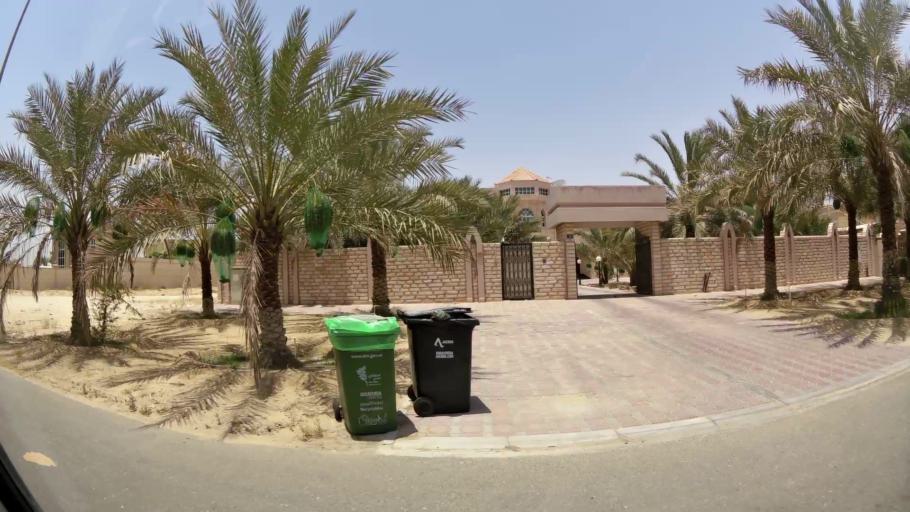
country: AE
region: Ash Shariqah
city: Sharjah
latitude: 25.2353
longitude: 55.4617
